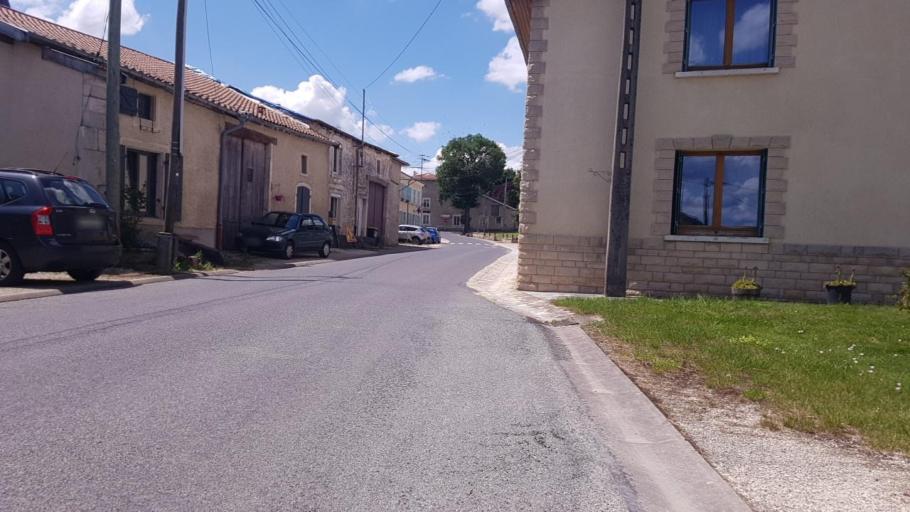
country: FR
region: Lorraine
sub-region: Departement de la Meuse
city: Vacon
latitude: 48.6624
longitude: 5.5479
